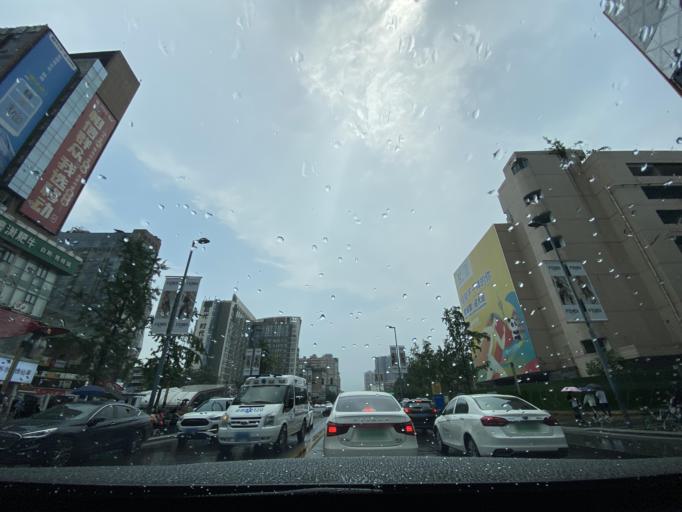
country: CN
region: Sichuan
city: Chengdu
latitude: 30.6558
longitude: 104.0764
